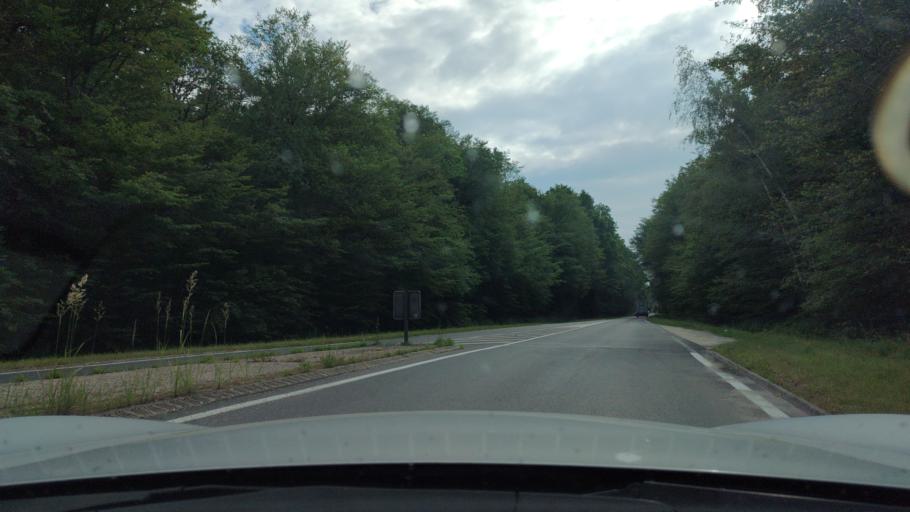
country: FR
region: Ile-de-France
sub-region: Departement de Seine-et-Marne
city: Villeneuve-le-Comte
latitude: 48.8151
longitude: 2.8428
